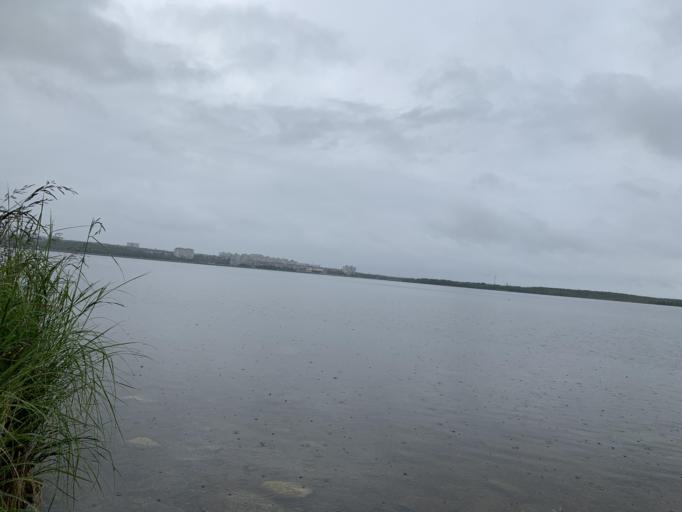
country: RU
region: Murmansk
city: Monchegorsk
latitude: 67.9375
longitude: 32.9912
